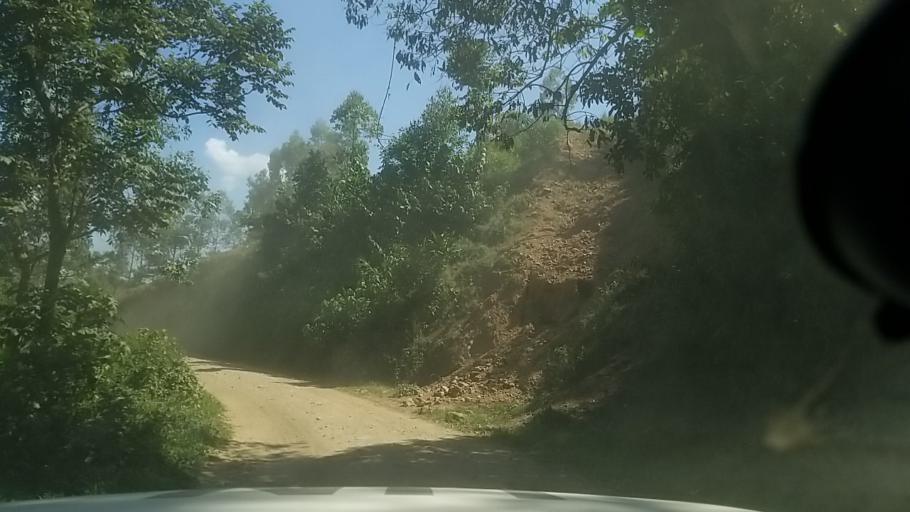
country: CD
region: Nord Kivu
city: Sake
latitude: -1.9517
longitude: 28.9275
